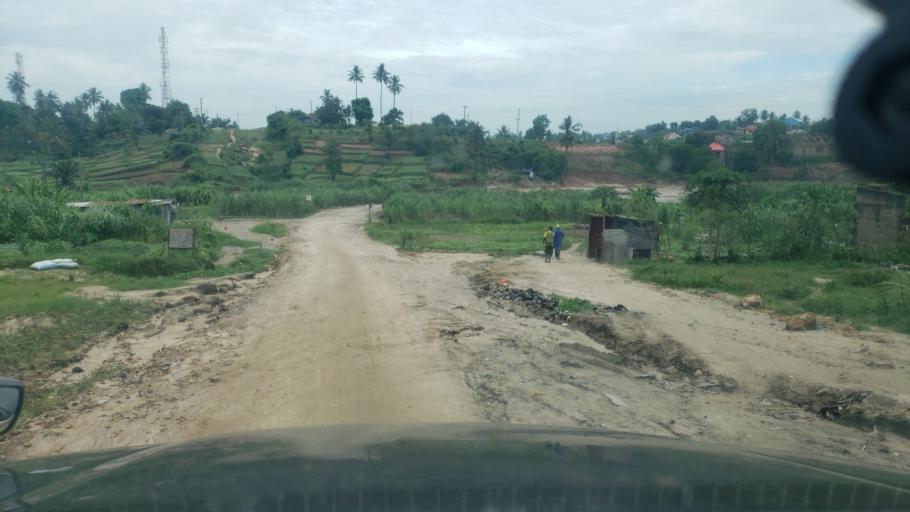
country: TZ
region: Dar es Salaam
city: Dar es Salaam
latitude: -6.9075
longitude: 39.2393
